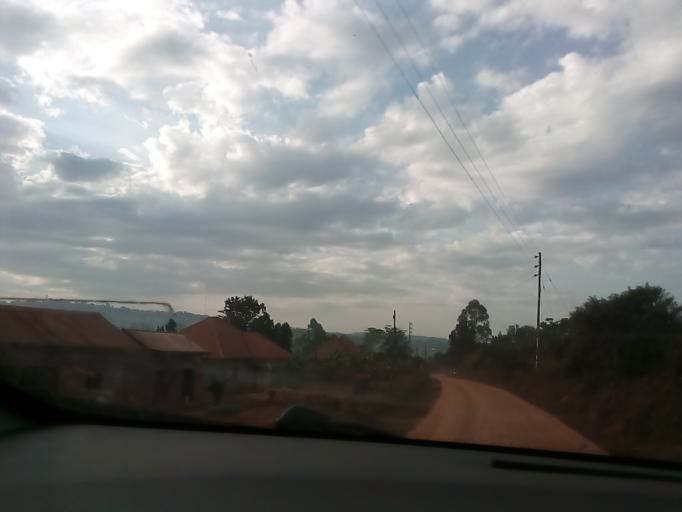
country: UG
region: Central Region
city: Masaka
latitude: -0.3523
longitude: 31.7198
